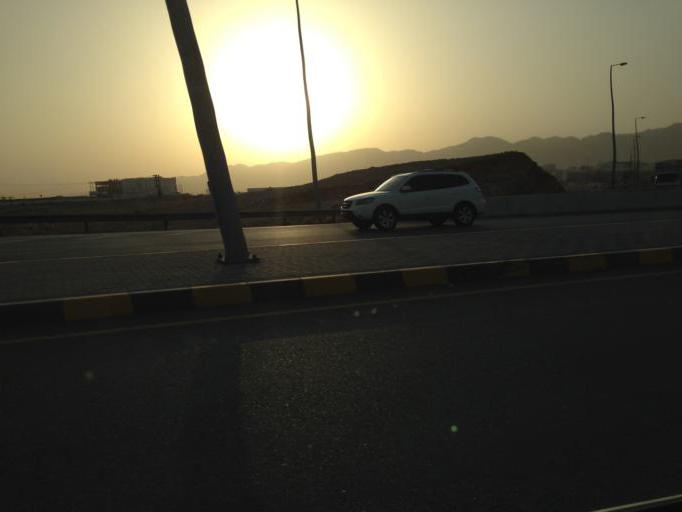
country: OM
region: Muhafazat Masqat
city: Bawshar
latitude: 23.5644
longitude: 58.3384
